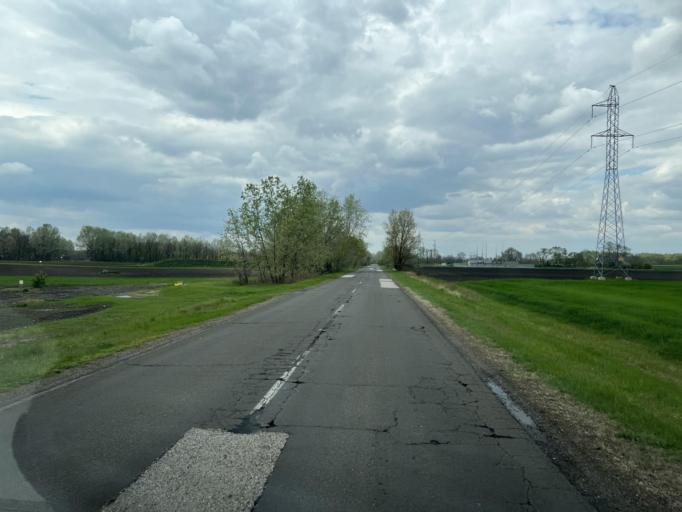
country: HU
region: Pest
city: Ujhartyan
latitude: 47.2028
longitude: 19.4020
